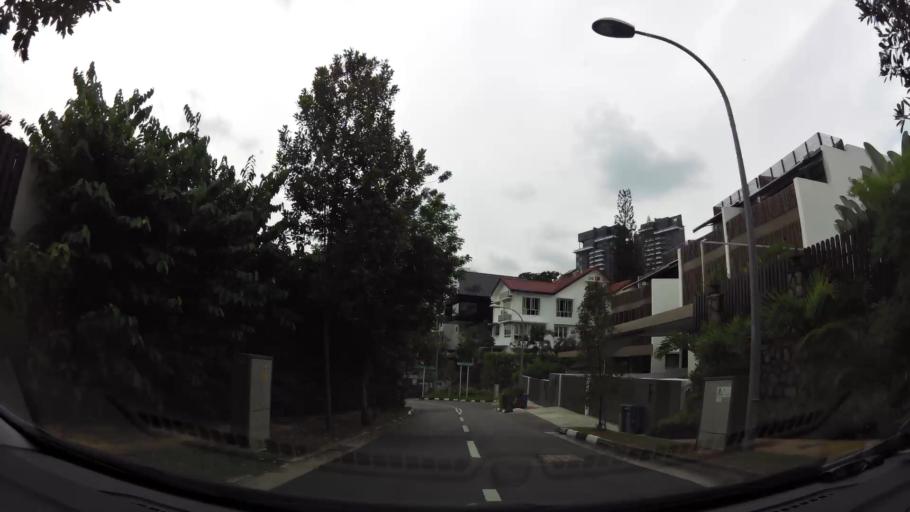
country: SG
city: Singapore
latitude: 1.3149
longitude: 103.7810
